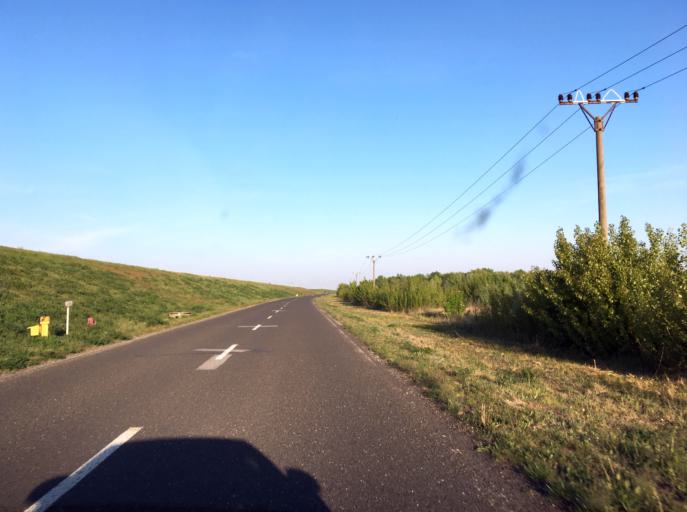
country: SK
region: Trnavsky
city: Samorin
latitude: 47.9970
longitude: 17.3277
